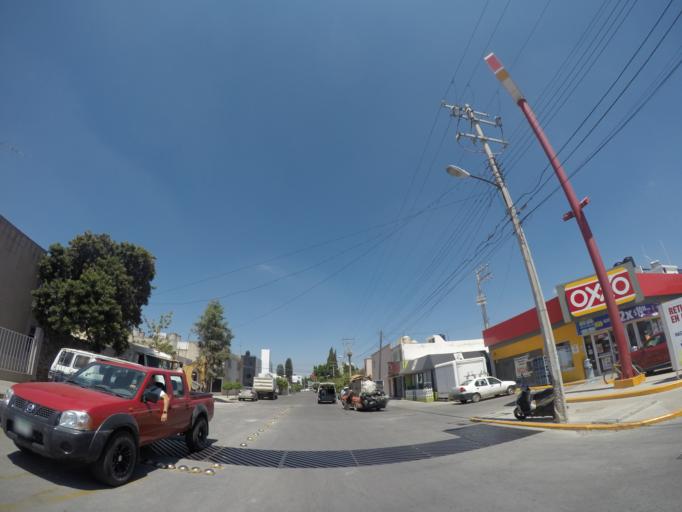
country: MX
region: San Luis Potosi
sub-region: San Luis Potosi
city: San Luis Potosi
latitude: 22.1466
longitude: -101.0016
